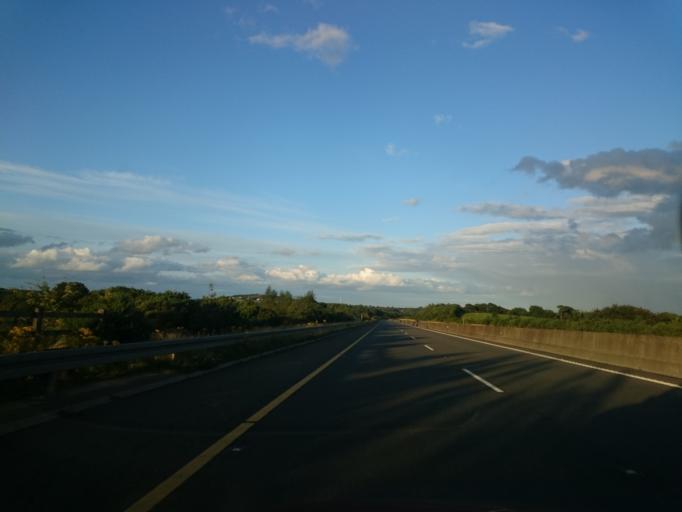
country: IE
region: Leinster
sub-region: Loch Garman
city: Gorey
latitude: 52.6343
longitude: -6.3591
